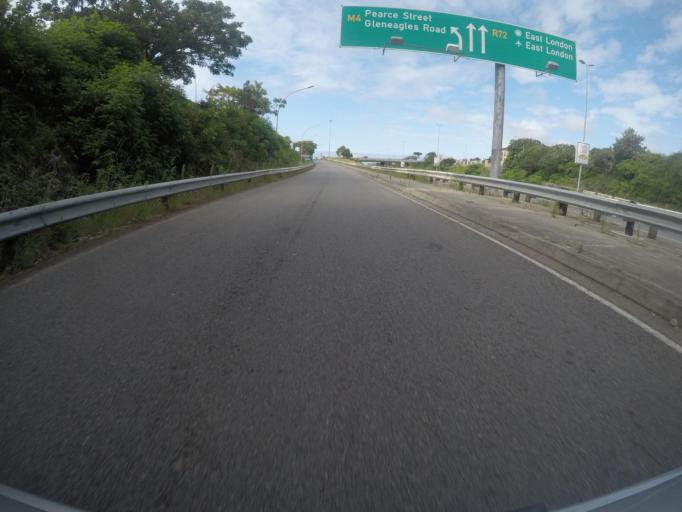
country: ZA
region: Eastern Cape
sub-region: Buffalo City Metropolitan Municipality
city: East London
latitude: -32.9917
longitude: 27.9189
